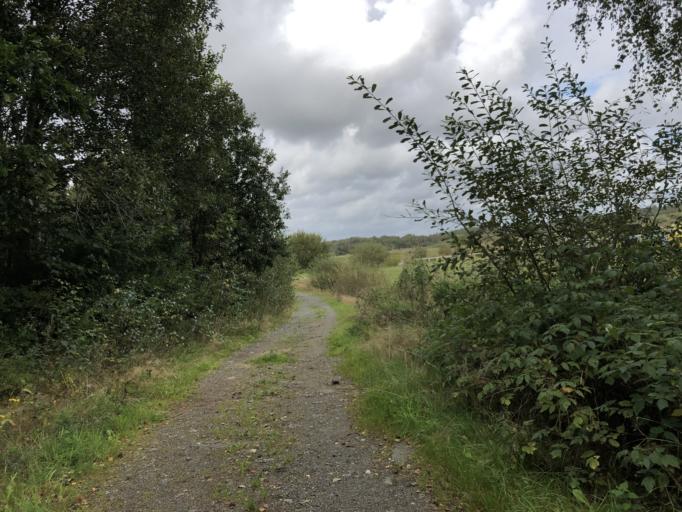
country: SE
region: Vaestra Goetaland
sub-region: Goteborg
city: Majorna
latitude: 57.7619
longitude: 11.8737
